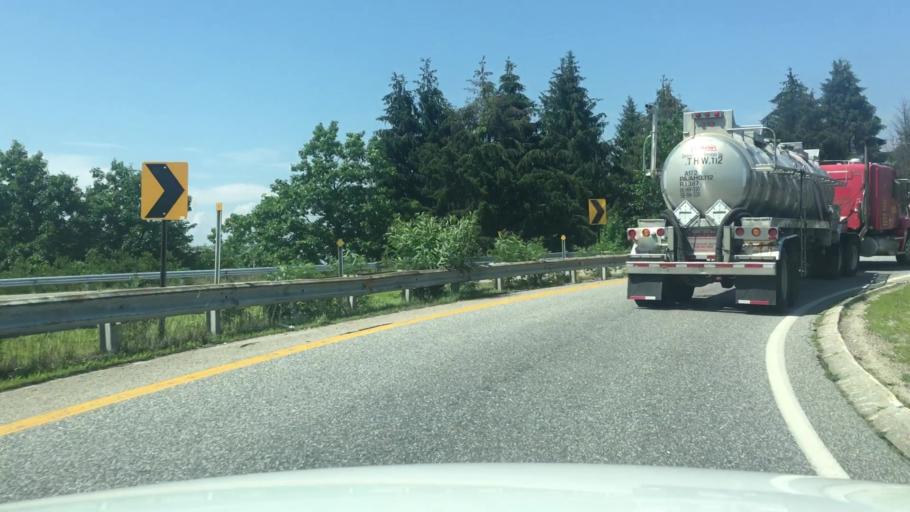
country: US
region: Maine
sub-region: Cumberland County
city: South Portland Gardens
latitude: 43.6387
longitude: -70.2960
